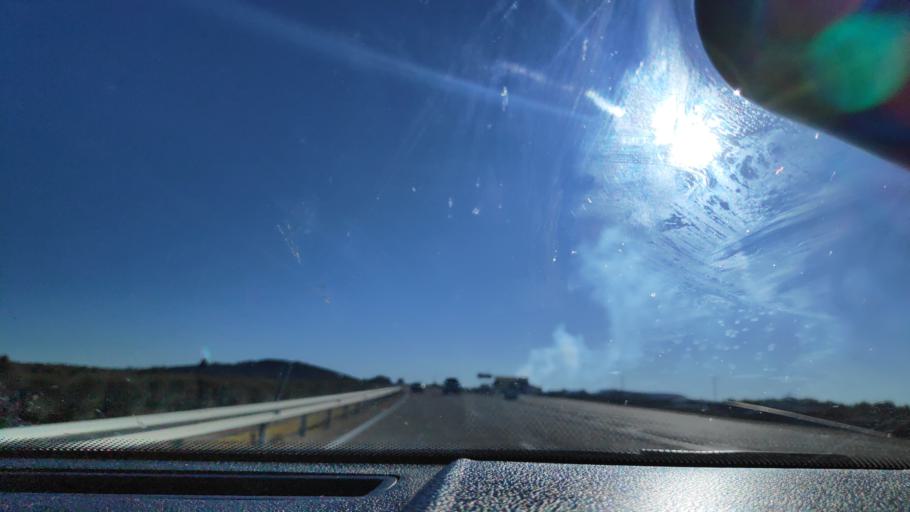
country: ES
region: Extremadura
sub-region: Provincia de Badajoz
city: Los Santos de Maimona
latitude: 38.4754
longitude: -6.3603
